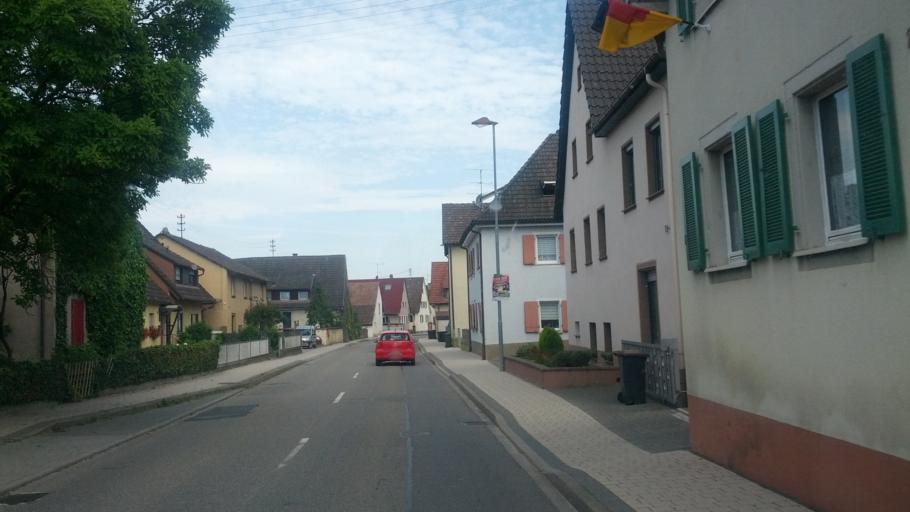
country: DE
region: Baden-Wuerttemberg
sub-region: Freiburg Region
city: Pfaffenweiler
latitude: 47.9194
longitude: 7.7446
